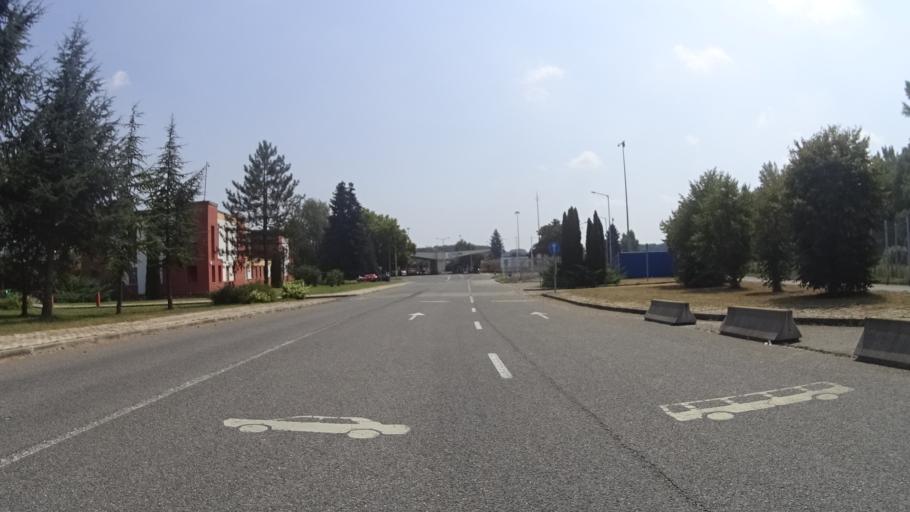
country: HU
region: Zala
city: Letenye
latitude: 46.4205
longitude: 16.6956
